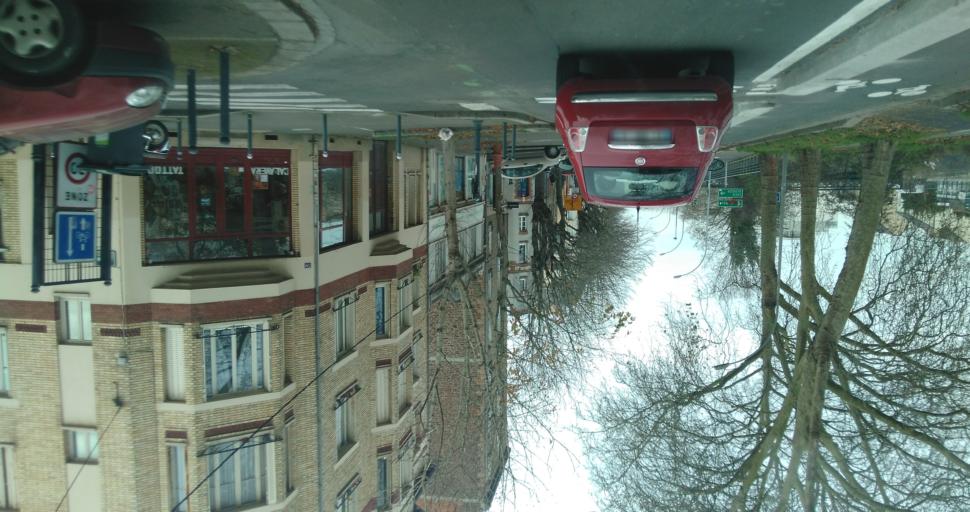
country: FR
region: Brittany
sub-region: Departement d'Ille-et-Vilaine
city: Rennes
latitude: 48.1167
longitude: -1.6863
